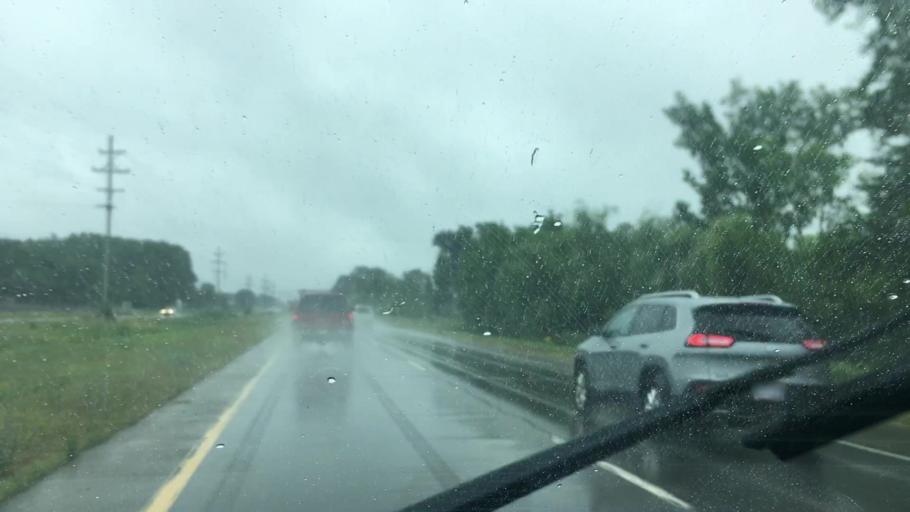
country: US
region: Michigan
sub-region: Ottawa County
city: Jenison
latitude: 42.8921
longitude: -85.8216
